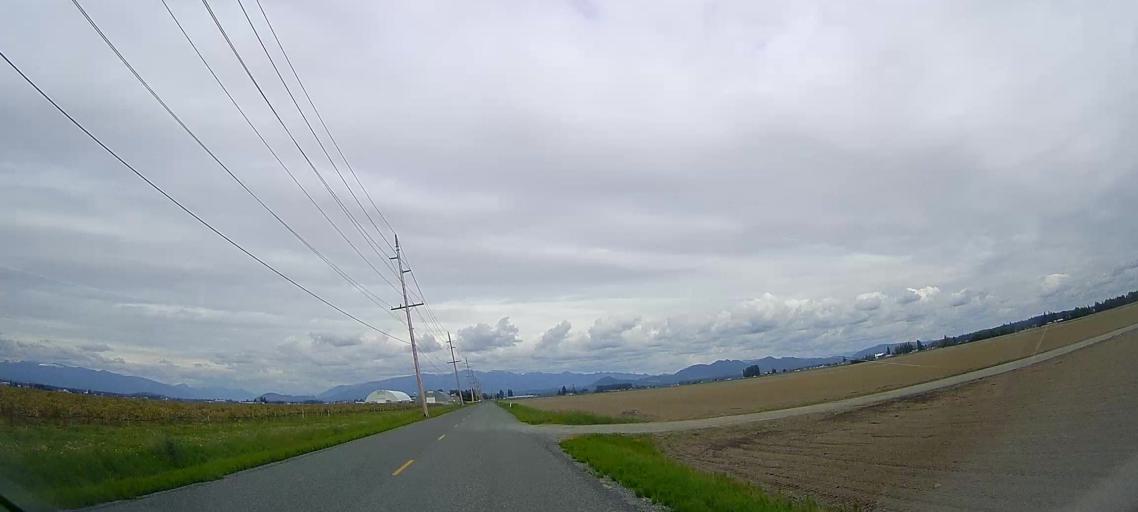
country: US
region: Washington
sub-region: Skagit County
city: Anacortes
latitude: 48.4209
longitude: -122.4960
